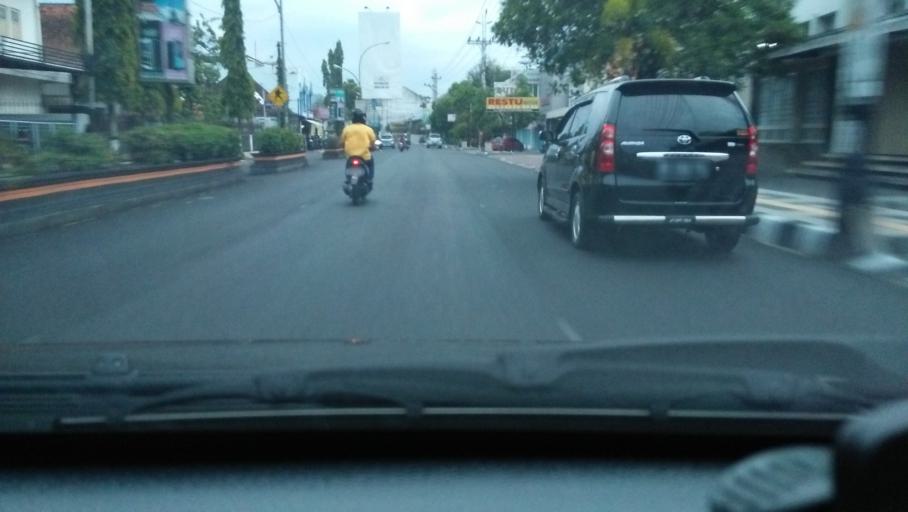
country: ID
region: Central Java
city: Magelang
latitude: -7.4708
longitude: 110.2178
